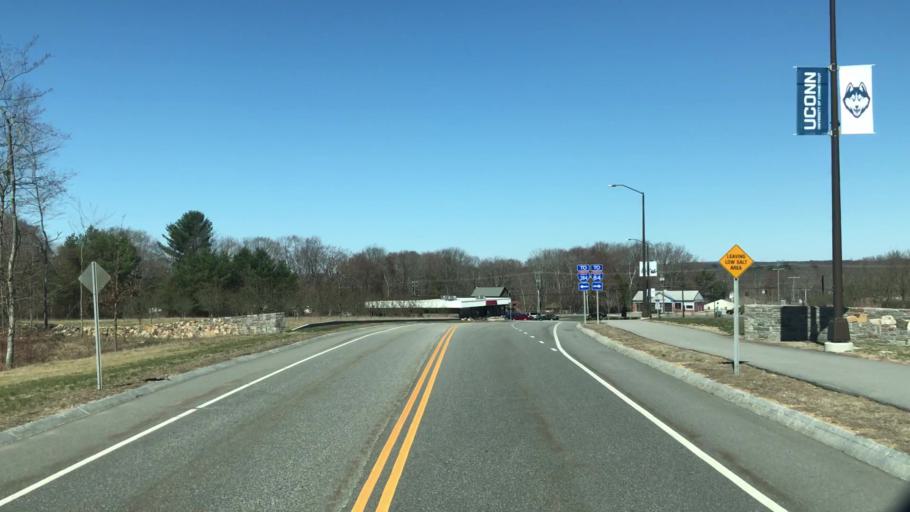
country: US
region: Connecticut
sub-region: Tolland County
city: Storrs
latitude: 41.8240
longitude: -72.2691
